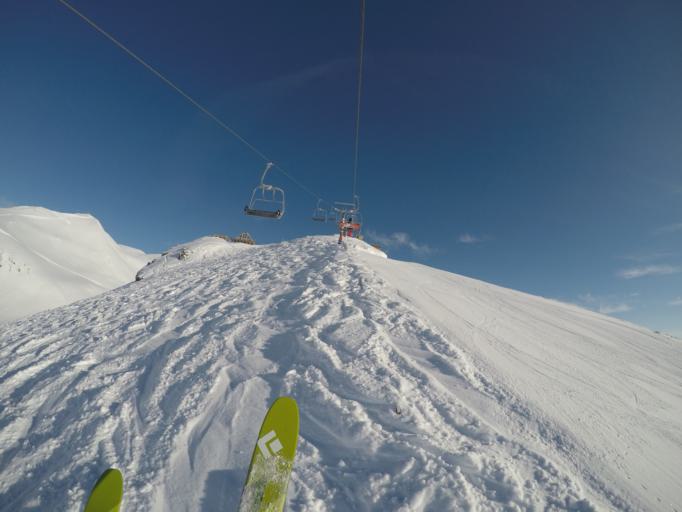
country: GE
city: Gudauri
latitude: 42.4961
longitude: 44.5068
